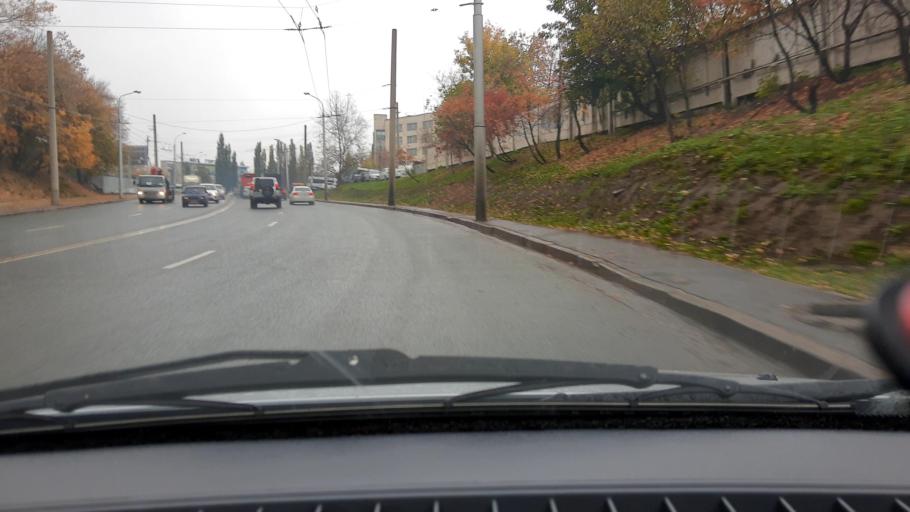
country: RU
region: Bashkortostan
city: Ufa
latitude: 54.7488
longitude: 55.9774
